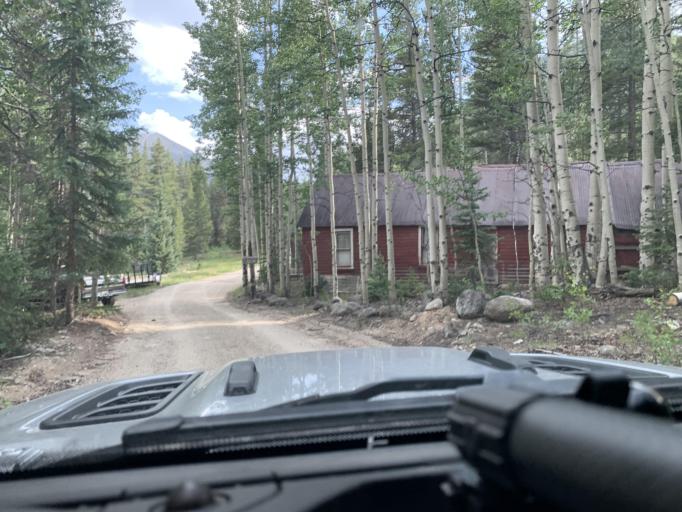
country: US
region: Colorado
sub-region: Chaffee County
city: Buena Vista
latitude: 38.7027
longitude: -106.3500
